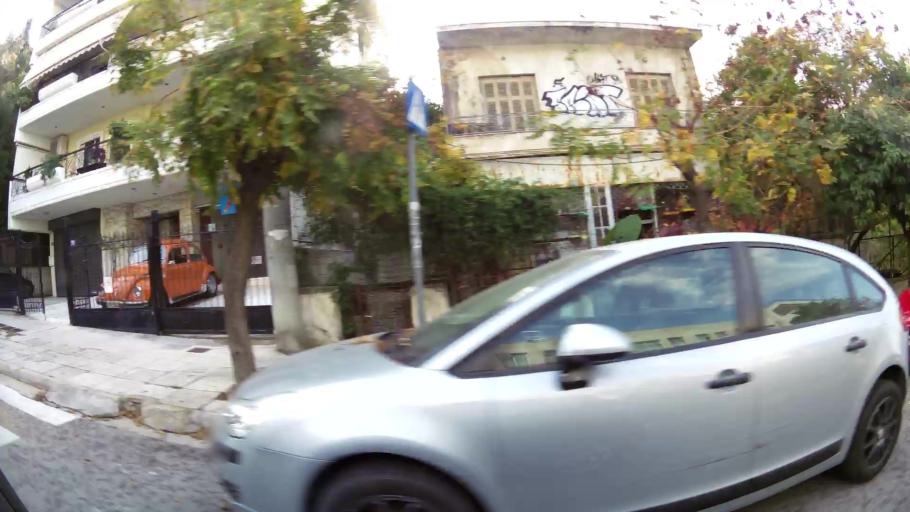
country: GR
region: Attica
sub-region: Nomarchia Athinas
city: Kipseli
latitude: 38.0097
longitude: 23.7412
